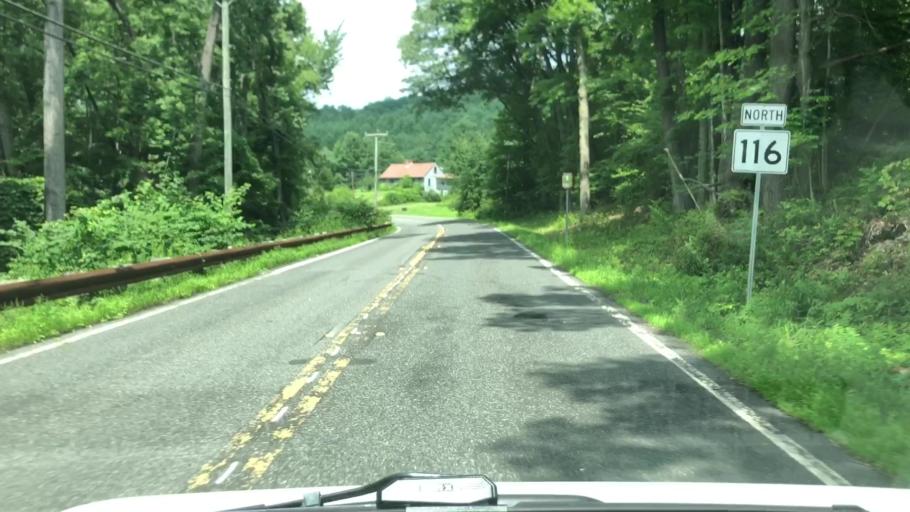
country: US
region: Massachusetts
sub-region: Franklin County
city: Conway
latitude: 42.5085
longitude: -72.7109
